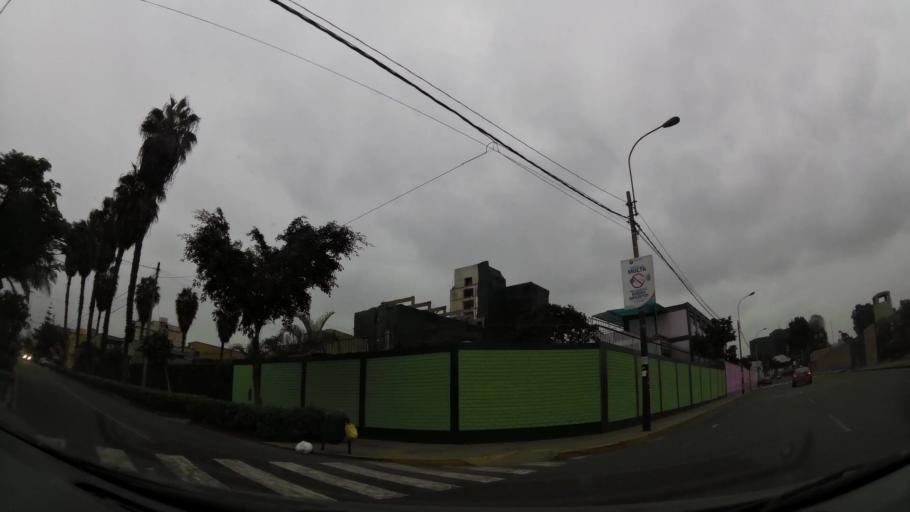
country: PE
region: Lima
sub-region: Lima
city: San Isidro
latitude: -12.0798
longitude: -77.0443
